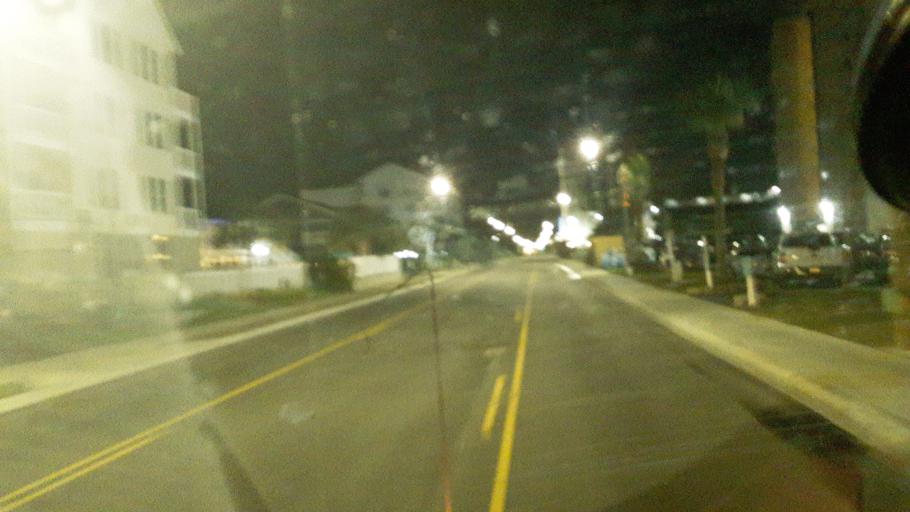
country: US
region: South Carolina
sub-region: Horry County
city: North Myrtle Beach
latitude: 33.8028
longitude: -78.7112
